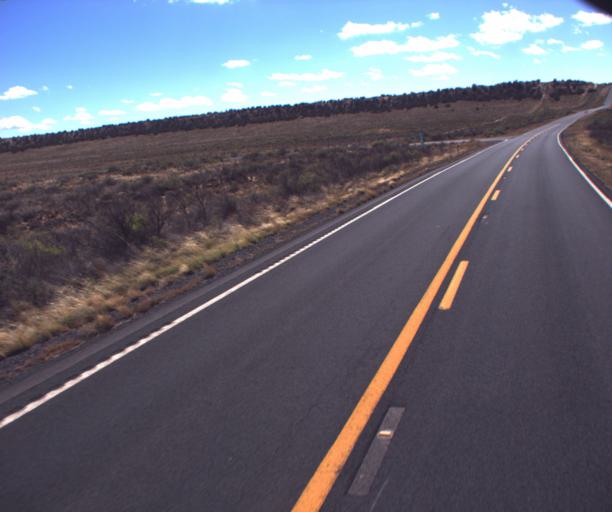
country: US
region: Arizona
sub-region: Apache County
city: Houck
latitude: 35.0983
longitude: -109.3130
